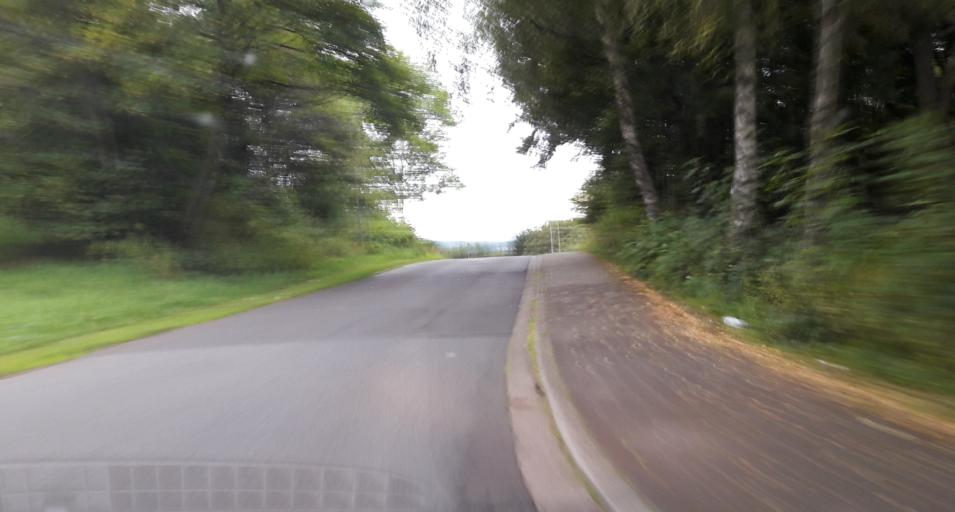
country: DE
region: Saarland
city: Tholey
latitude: 49.4927
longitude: 7.0369
